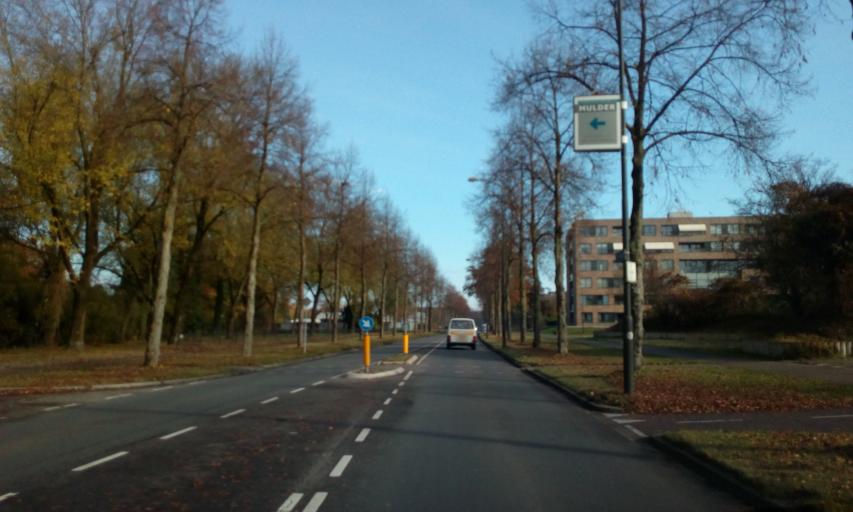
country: NL
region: Gelderland
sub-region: Gemeente Apeldoorn
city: Apeldoorn
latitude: 52.2026
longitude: 5.9512
